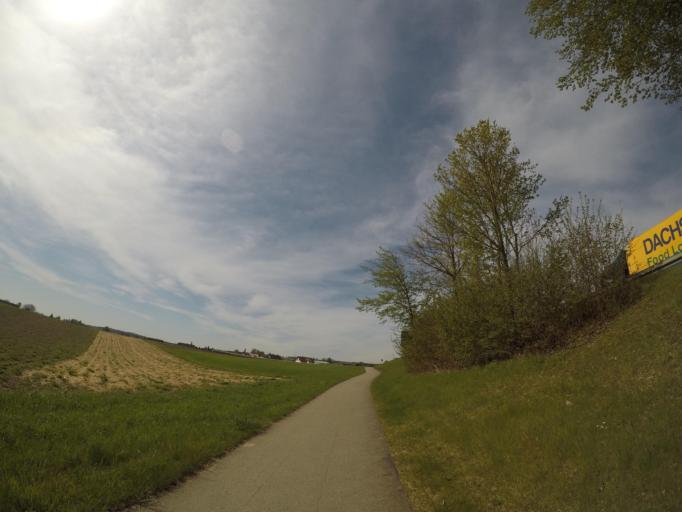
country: DE
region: Baden-Wuerttemberg
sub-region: Tuebingen Region
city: Boms
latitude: 47.9807
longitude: 9.5141
